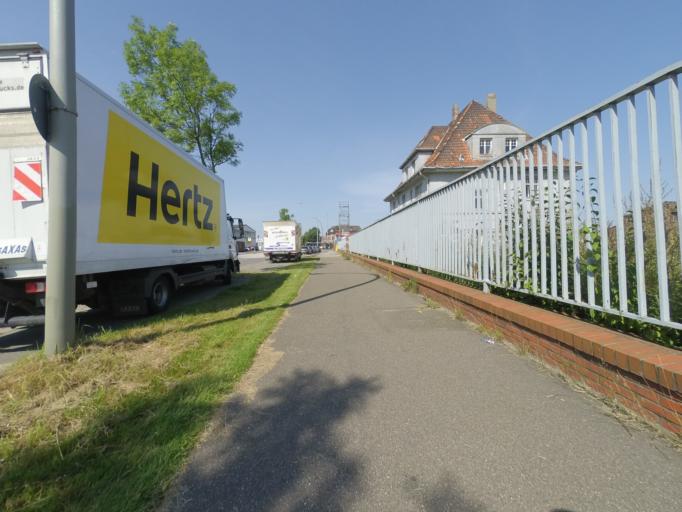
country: DE
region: Hamburg
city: Wandsbek
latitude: 53.5358
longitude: 10.1006
